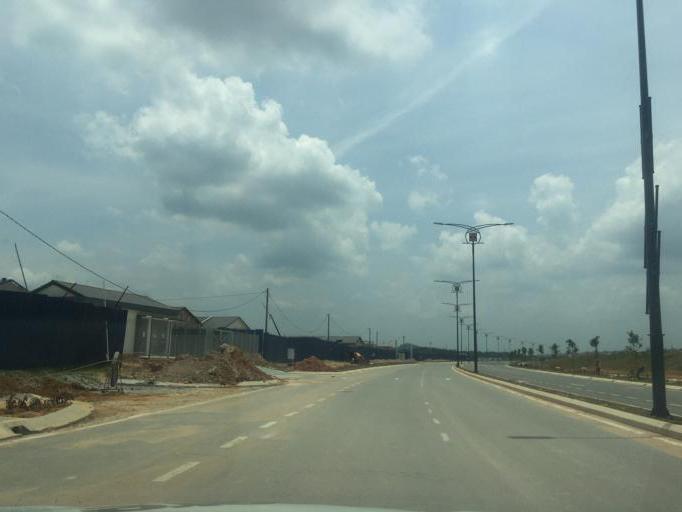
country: MY
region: Putrajaya
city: Putrajaya
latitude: 2.8492
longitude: 101.7053
